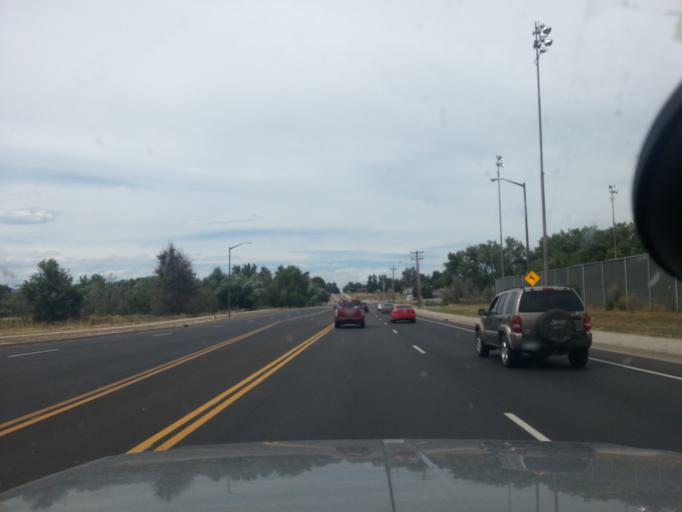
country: US
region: Colorado
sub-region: Larimer County
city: Loveland
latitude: 40.3935
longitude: -105.0968
